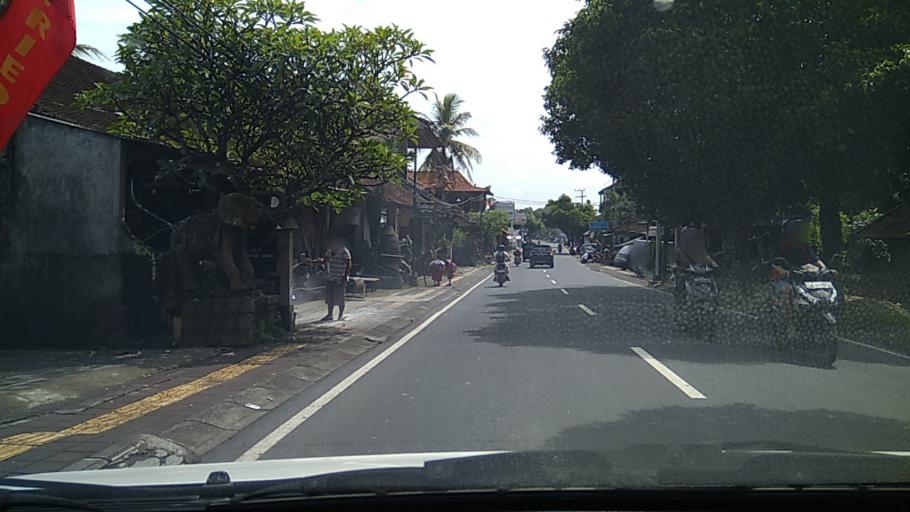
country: ID
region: Bali
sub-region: Kabupaten Gianyar
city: Ubud
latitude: -8.5239
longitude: 115.2719
